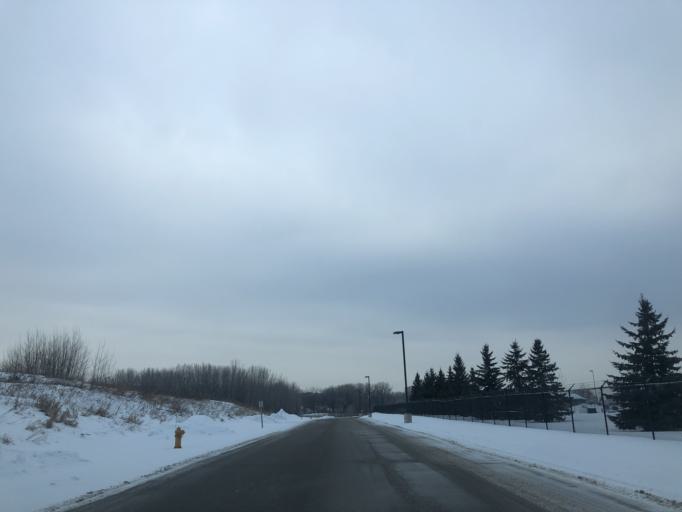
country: US
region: Minnesota
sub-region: Ramsey County
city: Shoreview
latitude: 45.0815
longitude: -93.1638
